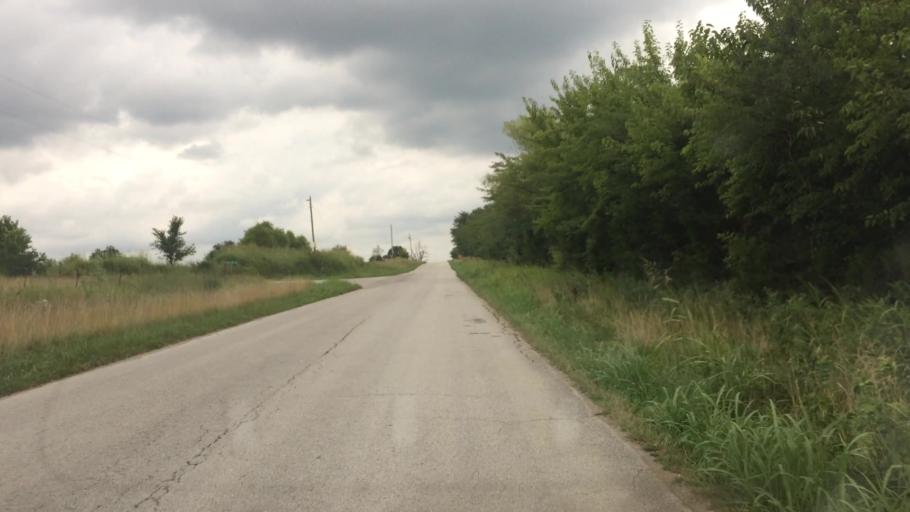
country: US
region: Missouri
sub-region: Greene County
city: Strafford
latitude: 37.3163
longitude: -93.0663
